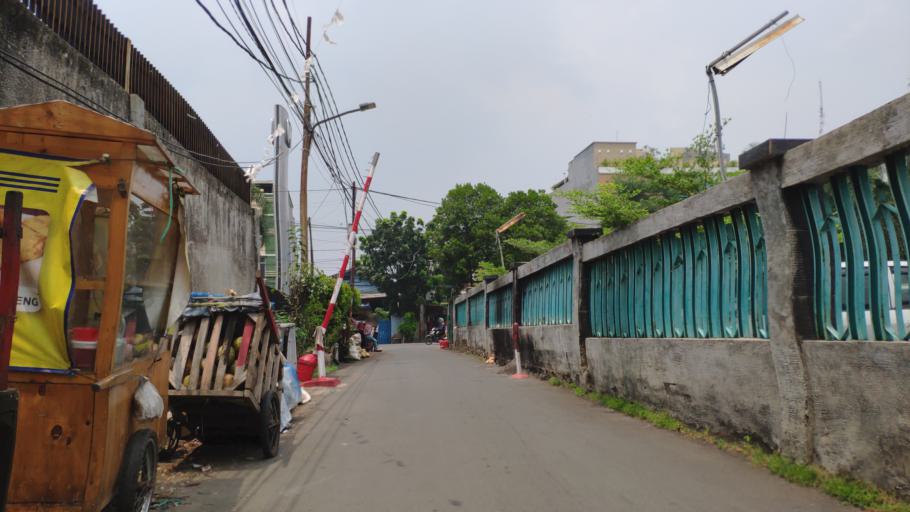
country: ID
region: Banten
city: South Tangerang
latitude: -6.2706
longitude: 106.7757
